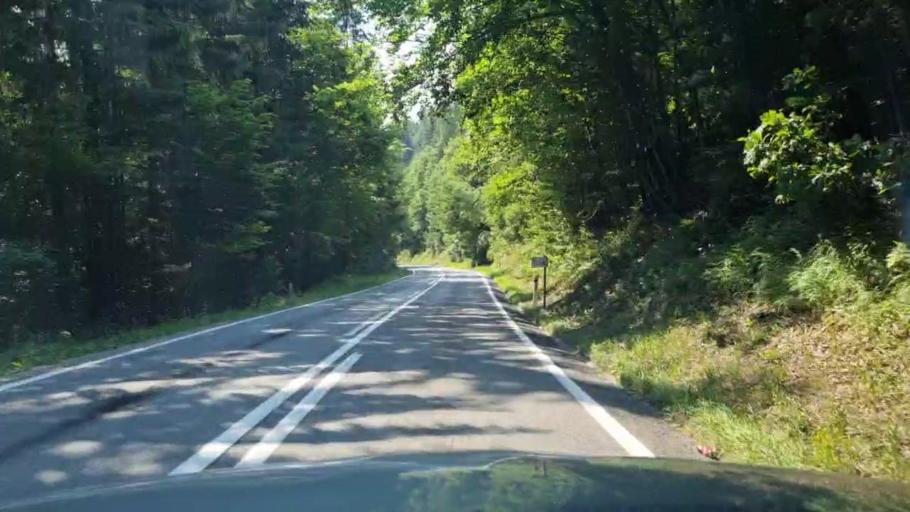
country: BA
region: Federation of Bosnia and Herzegovina
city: Olovo
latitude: 44.1612
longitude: 18.6492
